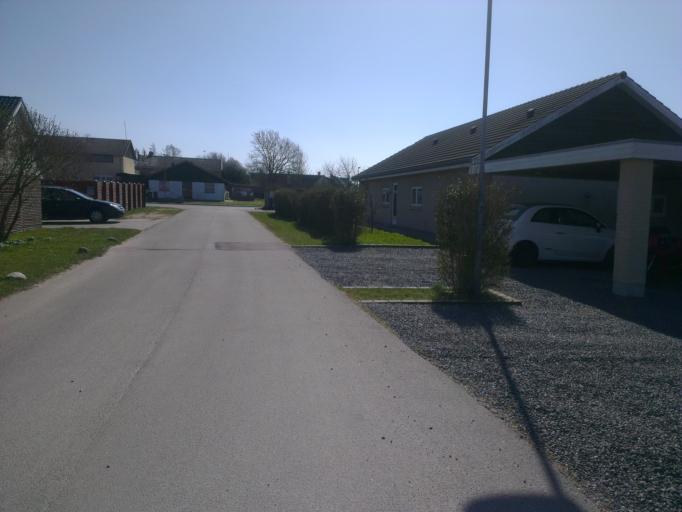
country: DK
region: Capital Region
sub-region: Frederikssund Kommune
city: Frederikssund
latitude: 55.8529
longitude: 12.0642
